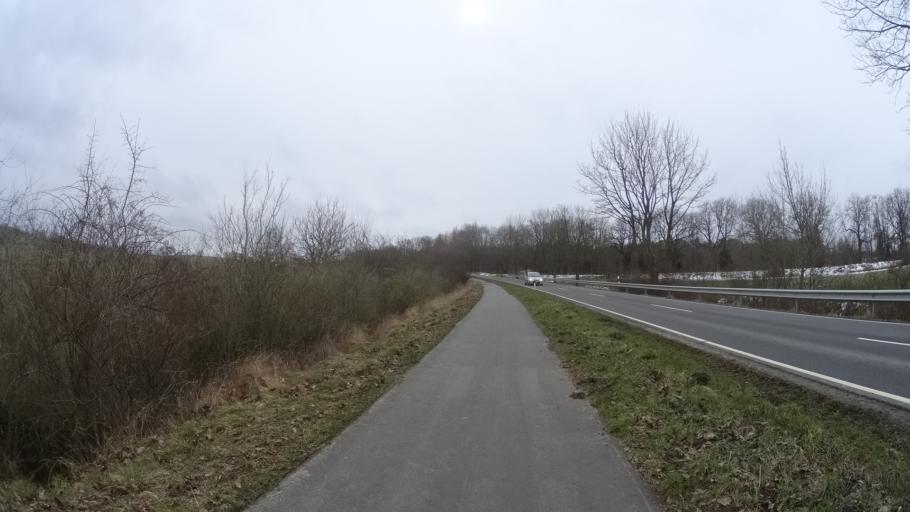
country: DE
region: Schleswig-Holstein
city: Panker
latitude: 54.3407
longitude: 10.5586
